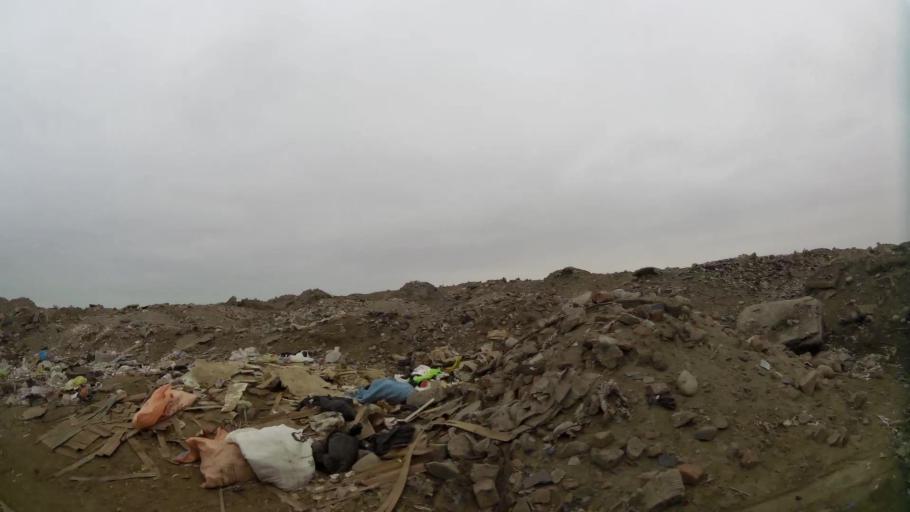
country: PE
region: Ica
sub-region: Provincia de Pisco
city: Pisco
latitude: -13.7524
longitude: -76.1894
